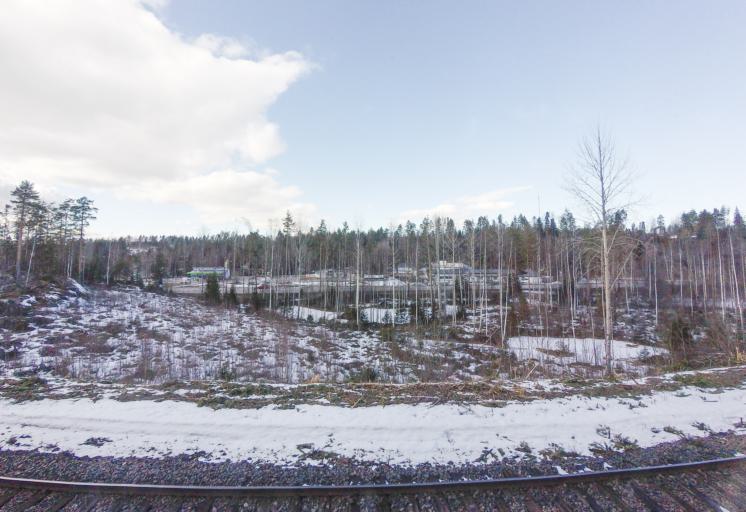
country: FI
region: South Karelia
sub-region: Imatra
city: Simpele
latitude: 61.4240
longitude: 29.3635
